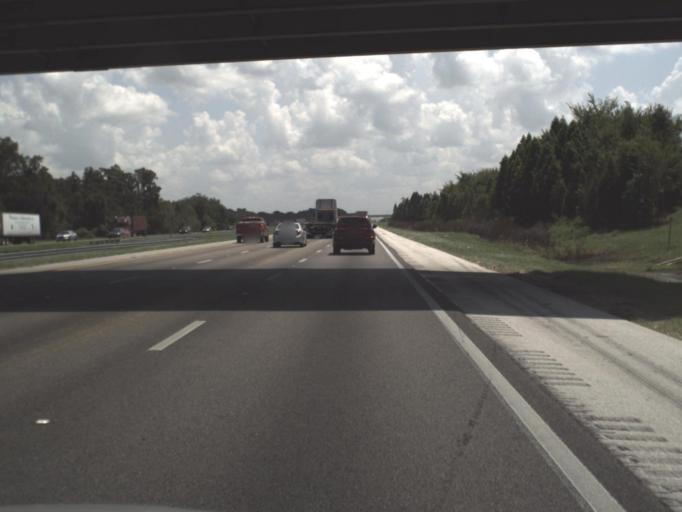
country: US
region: Florida
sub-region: Hillsborough County
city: Dover
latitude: 28.0274
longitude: -82.2162
